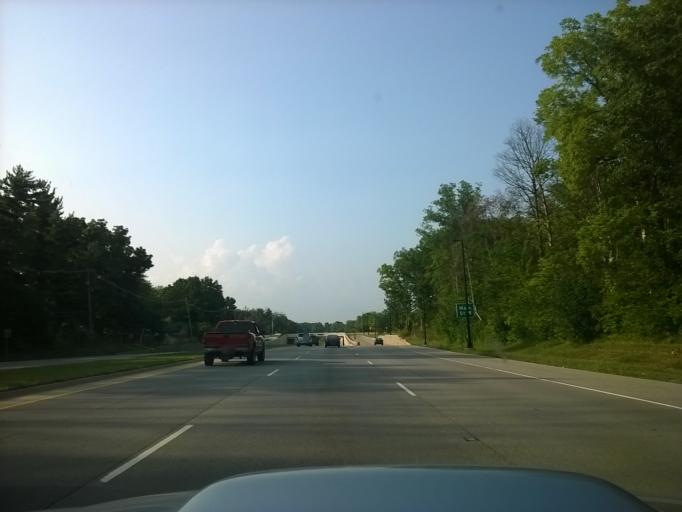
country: US
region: Indiana
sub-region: Hamilton County
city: Carmel
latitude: 39.9755
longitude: -86.1127
